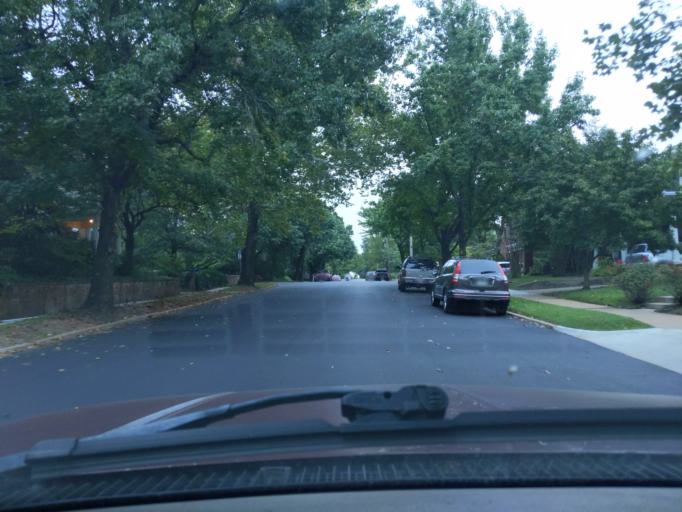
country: US
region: Oklahoma
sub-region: Tulsa County
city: Tulsa
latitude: 36.1355
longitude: -95.9732
